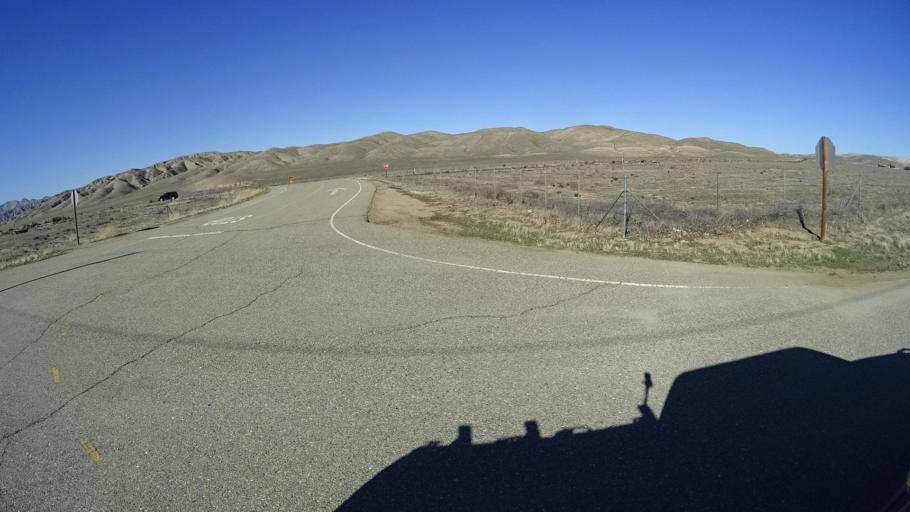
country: US
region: California
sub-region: Kern County
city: Maricopa
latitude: 34.9379
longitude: -119.4676
